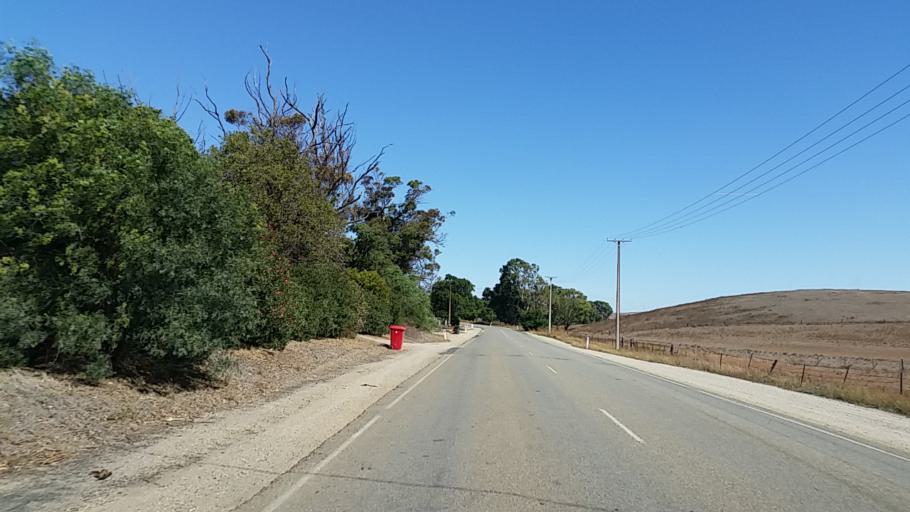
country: AU
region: South Australia
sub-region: Clare and Gilbert Valleys
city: Clare
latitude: -33.6744
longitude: 138.9182
